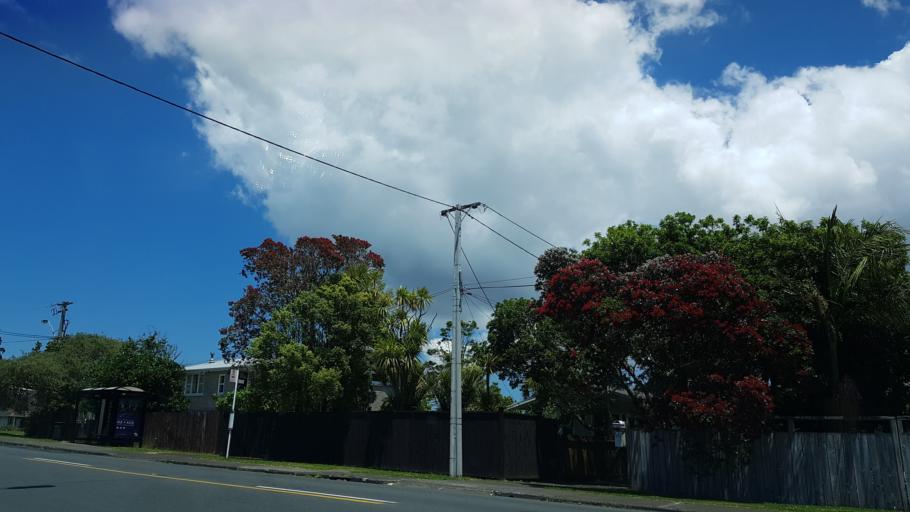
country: NZ
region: Auckland
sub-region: Auckland
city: North Shore
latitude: -36.8011
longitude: 174.6913
